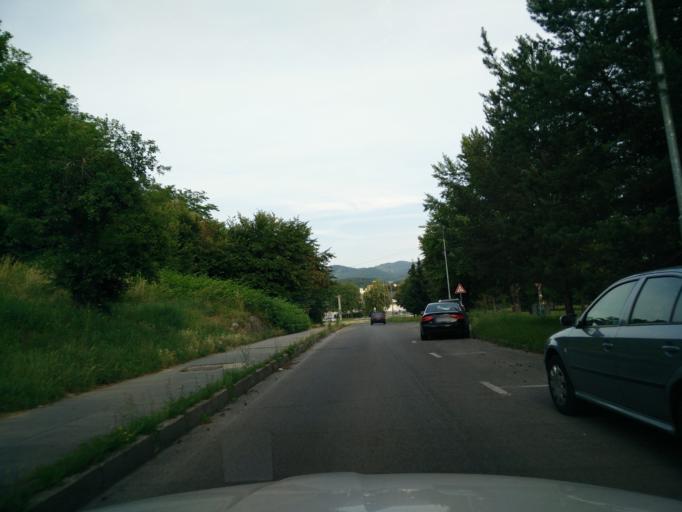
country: SK
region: Nitriansky
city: Prievidza
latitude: 48.7703
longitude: 18.6331
